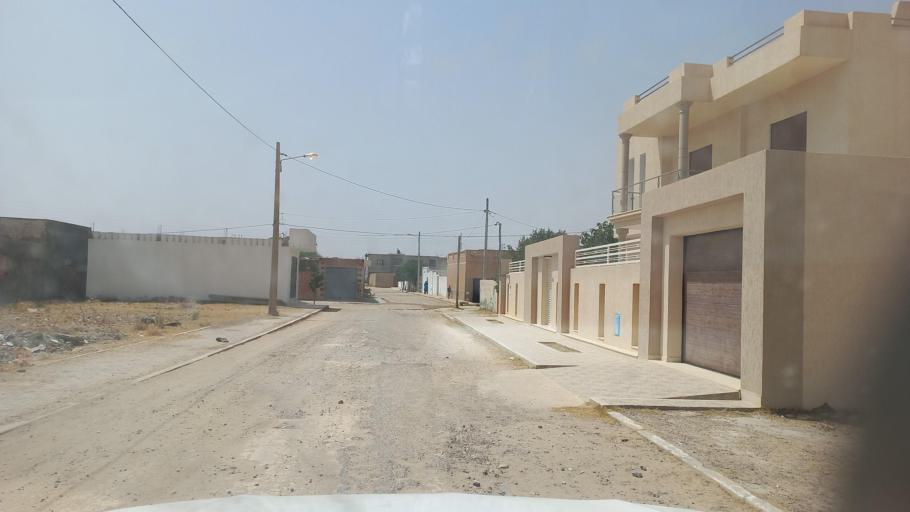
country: TN
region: Al Qasrayn
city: Kasserine
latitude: 35.2510
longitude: 9.0270
